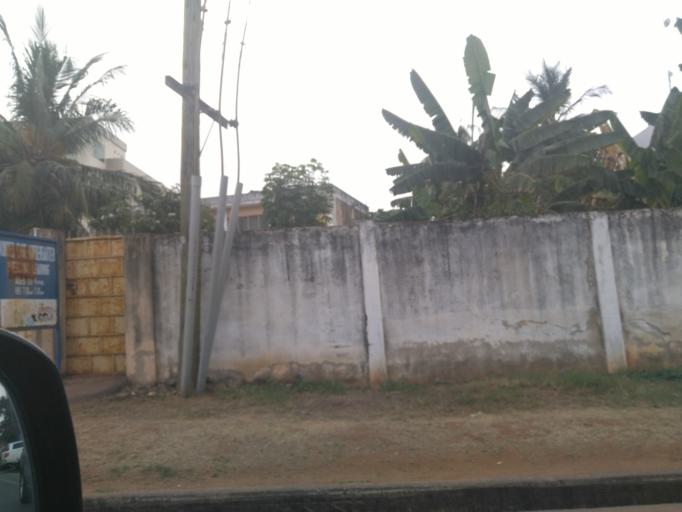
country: GH
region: Greater Accra
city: Accra
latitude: 5.6019
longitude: -0.1926
